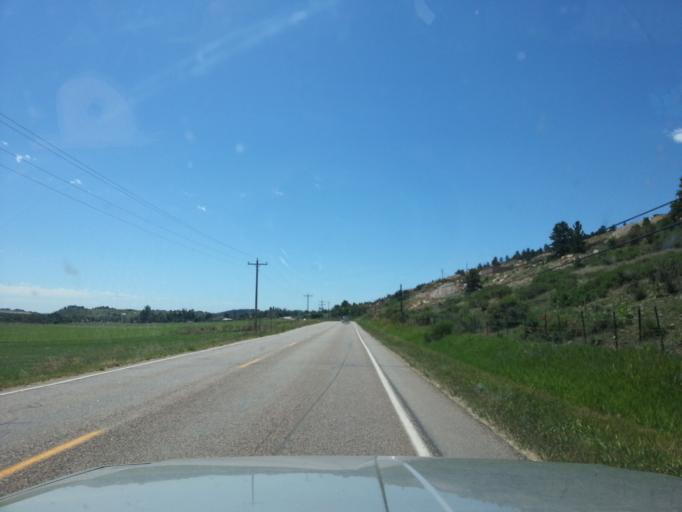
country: US
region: Colorado
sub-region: Larimer County
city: Loveland
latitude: 40.4474
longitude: -105.2031
